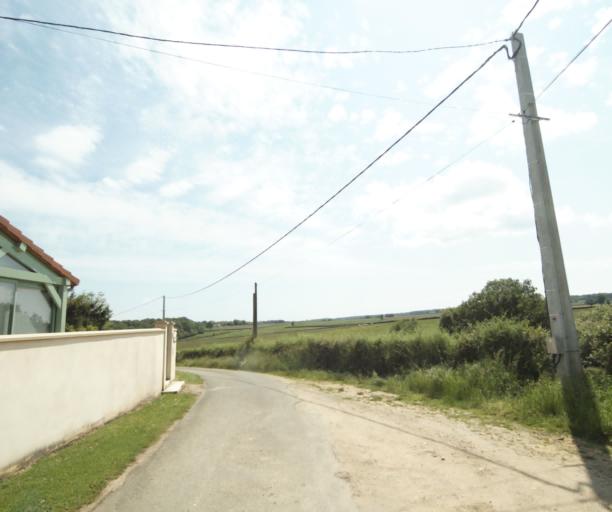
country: FR
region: Bourgogne
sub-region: Departement de Saone-et-Loire
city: Gueugnon
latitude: 46.5845
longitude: 4.1334
